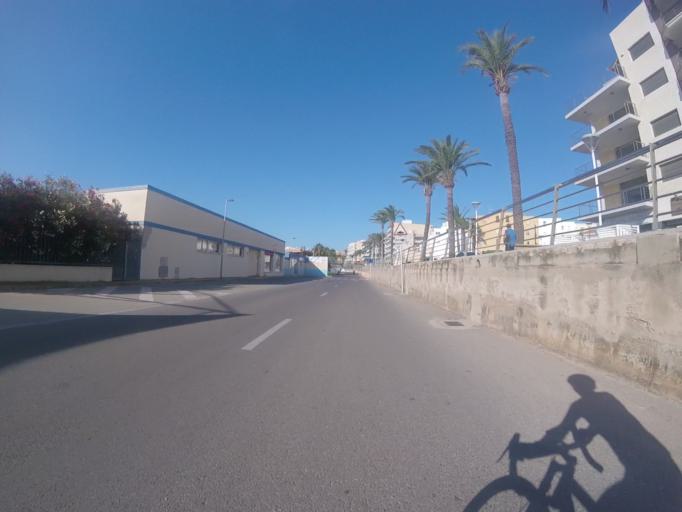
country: ES
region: Valencia
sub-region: Provincia de Castello
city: Benicarlo
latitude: 40.4166
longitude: 0.4343
